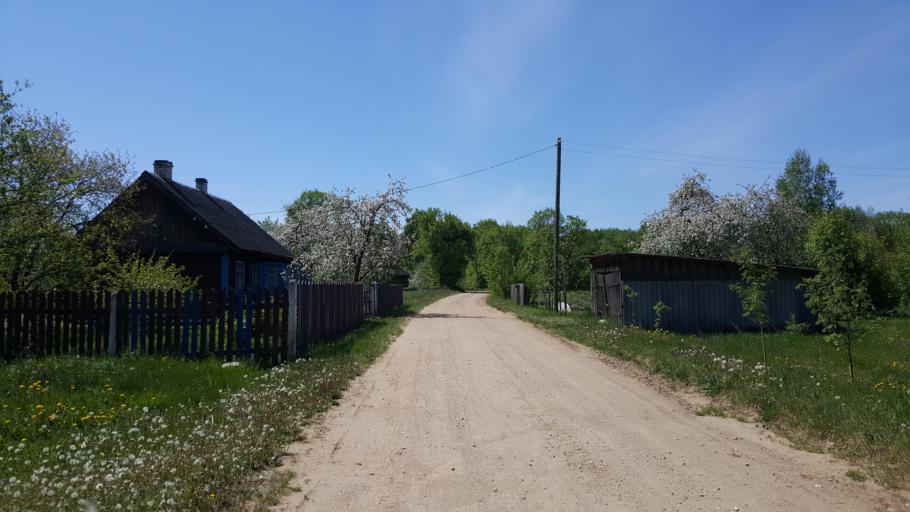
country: BY
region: Brest
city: Zhabinka
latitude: 52.3846
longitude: 24.0236
